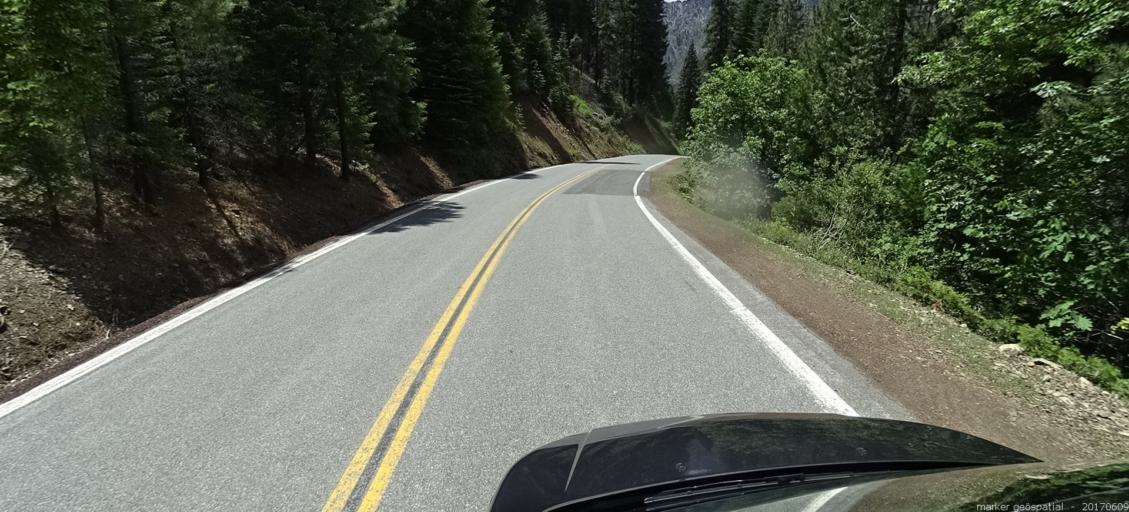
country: US
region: California
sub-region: Siskiyou County
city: Yreka
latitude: 41.3760
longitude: -123.0087
